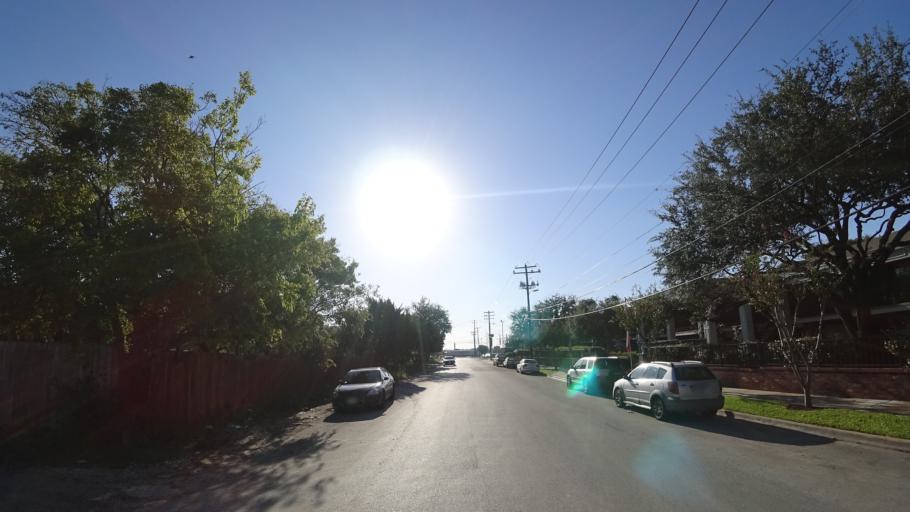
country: US
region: Texas
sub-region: Travis County
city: Austin
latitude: 30.3439
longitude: -97.6996
